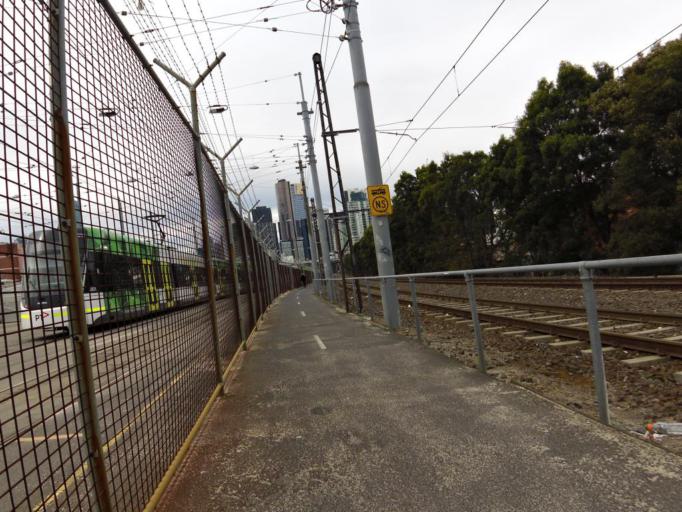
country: AU
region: Victoria
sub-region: Port Phillip
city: Port Melbourne
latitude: -37.8295
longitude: 144.9497
